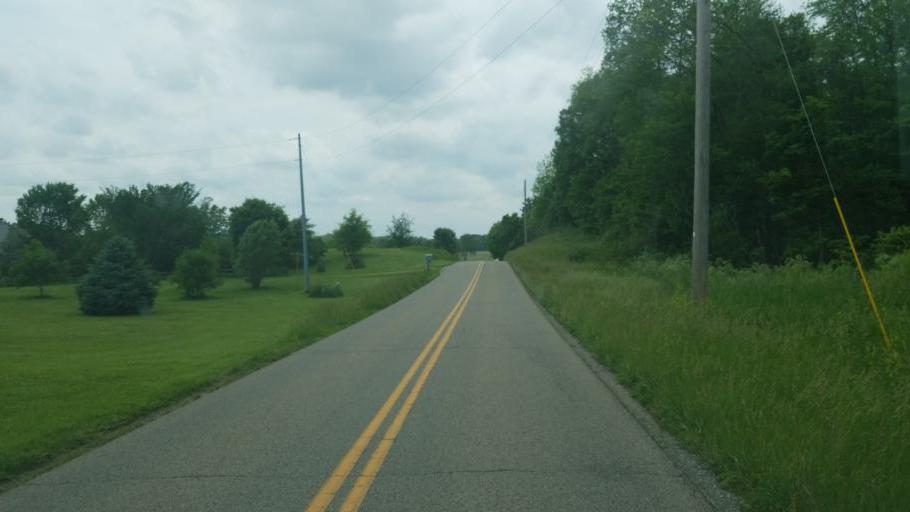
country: US
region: Ohio
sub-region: Perry County
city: Thornport
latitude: 39.9201
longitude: -82.3759
